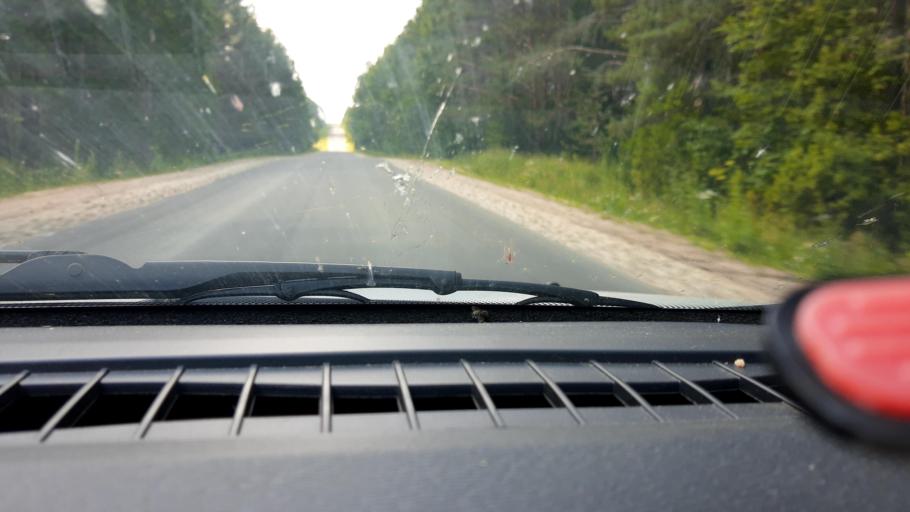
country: RU
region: Nizjnij Novgorod
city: Prudy
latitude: 57.3864
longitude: 46.1124
